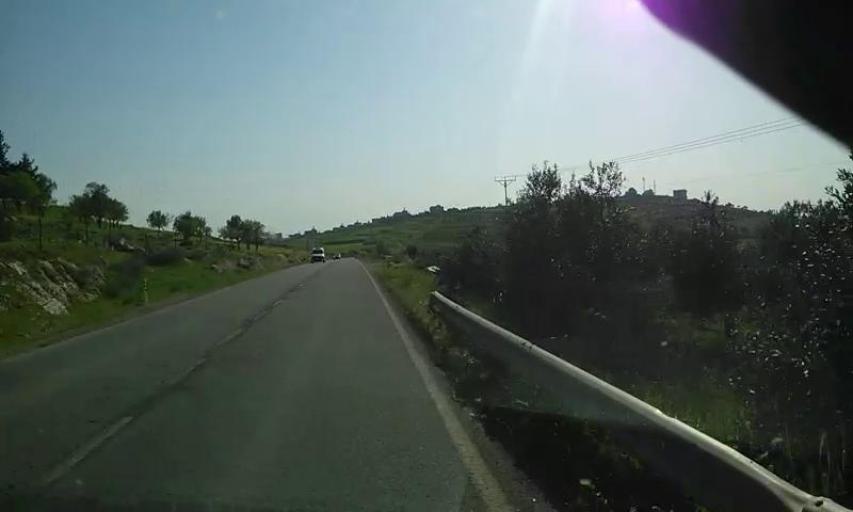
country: PS
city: Al Hilah
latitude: 31.4750
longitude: 35.1323
